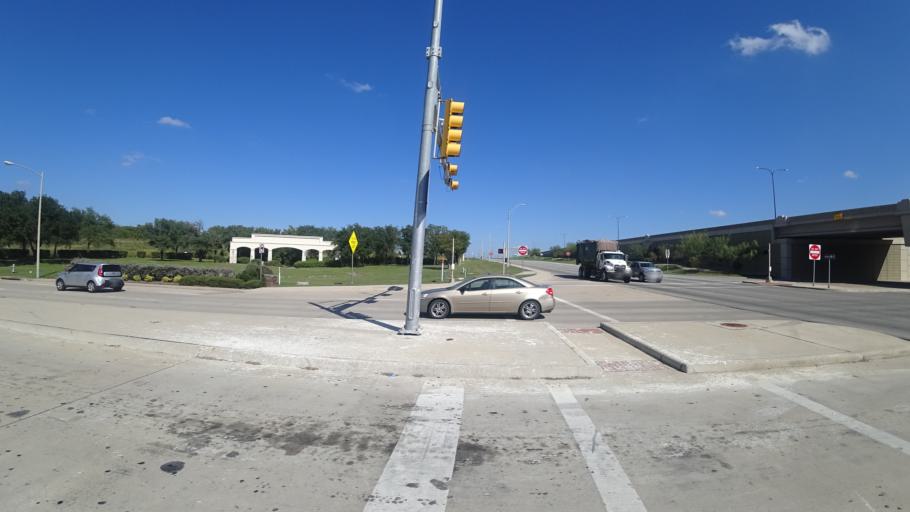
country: US
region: Texas
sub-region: Travis County
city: Manor
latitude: 30.3352
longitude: -97.6077
